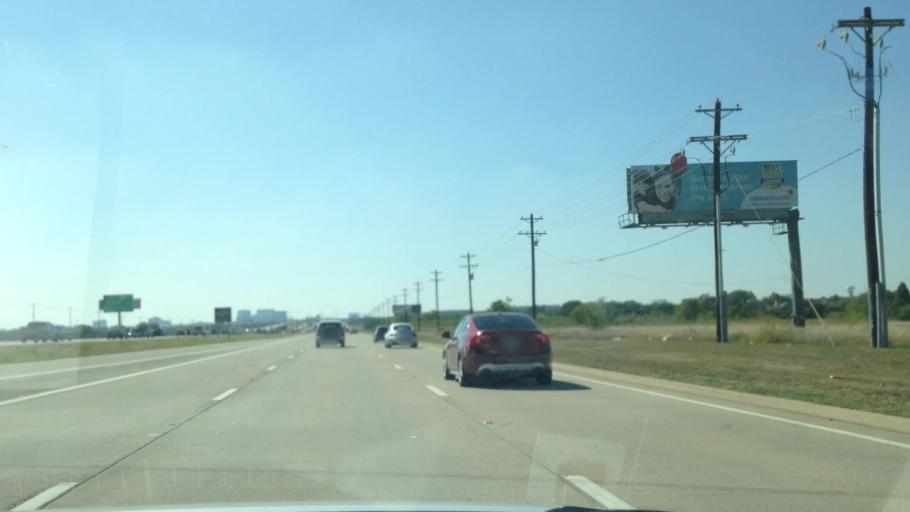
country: US
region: Texas
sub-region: Collin County
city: Frisco
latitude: 33.1099
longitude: -96.7753
